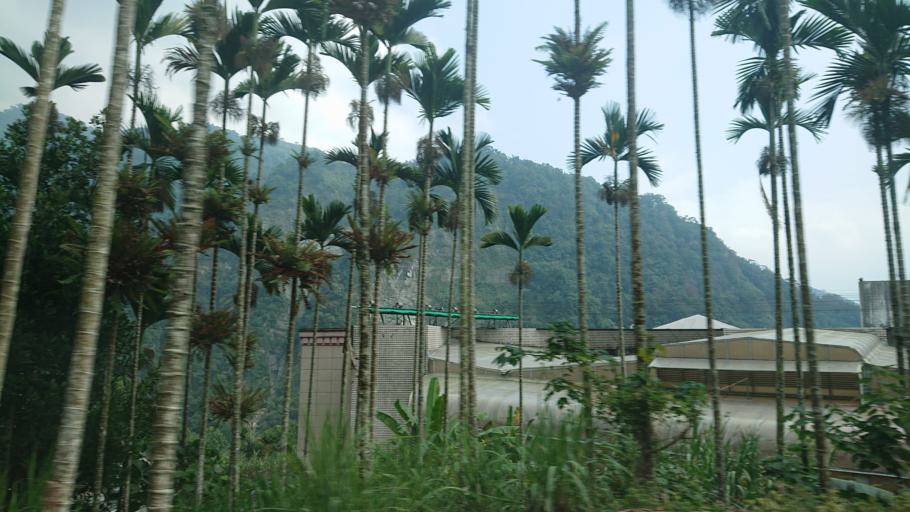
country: TW
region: Taiwan
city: Lugu
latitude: 23.5905
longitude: 120.6996
